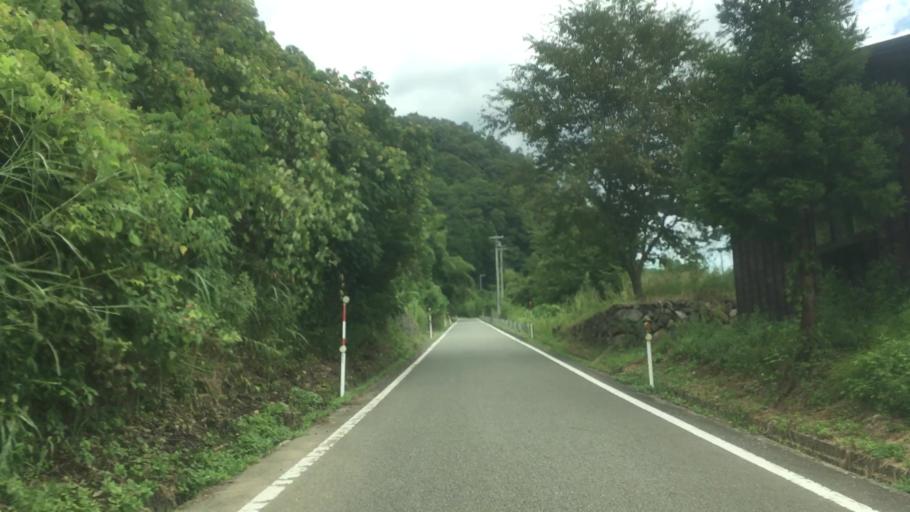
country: JP
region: Hyogo
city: Toyooka
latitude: 35.5814
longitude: 134.7992
